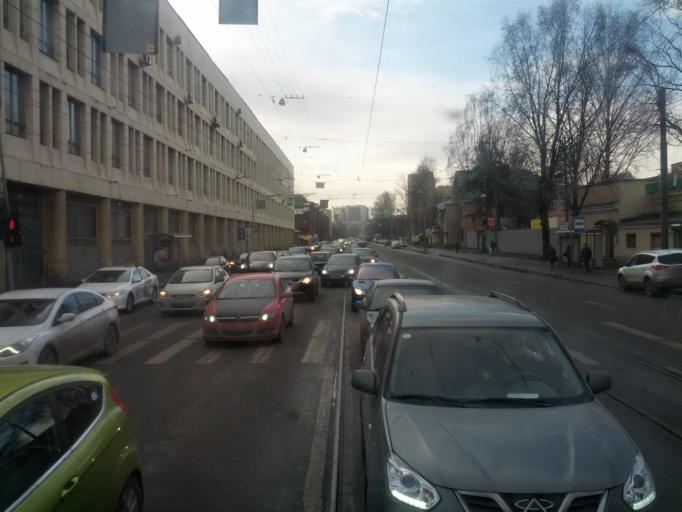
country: RU
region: St.-Petersburg
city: Centralniy
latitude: 59.9416
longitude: 30.4087
